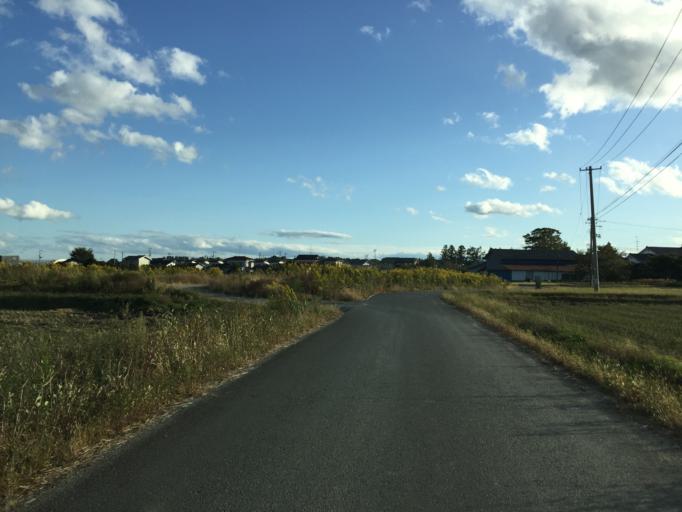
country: JP
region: Miyagi
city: Marumori
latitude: 37.7912
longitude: 140.9530
